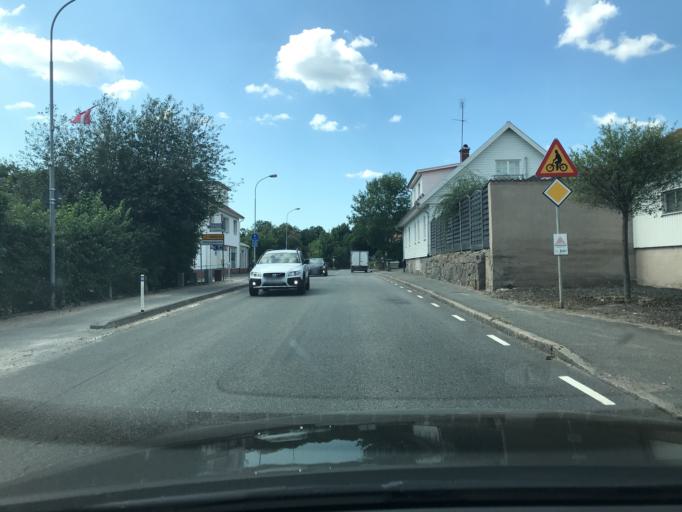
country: SE
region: Skane
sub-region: Hassleholms Kommun
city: Hastveda
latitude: 56.2858
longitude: 13.9323
